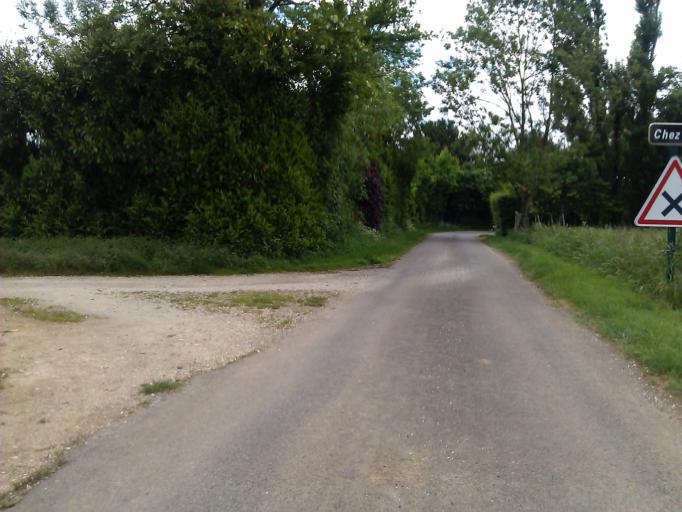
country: FR
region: Poitou-Charentes
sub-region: Departement de la Charente
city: Nanteuil-en-Vallee
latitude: 45.9571
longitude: 0.2541
